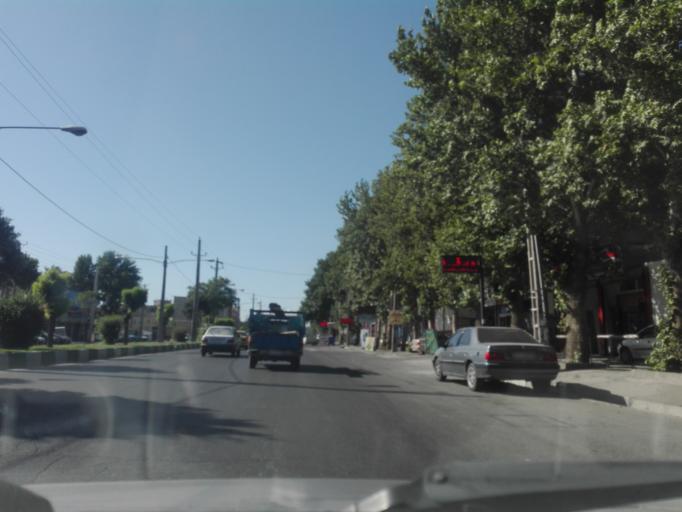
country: IR
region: Tehran
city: Shahriar
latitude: 35.6378
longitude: 51.0648
